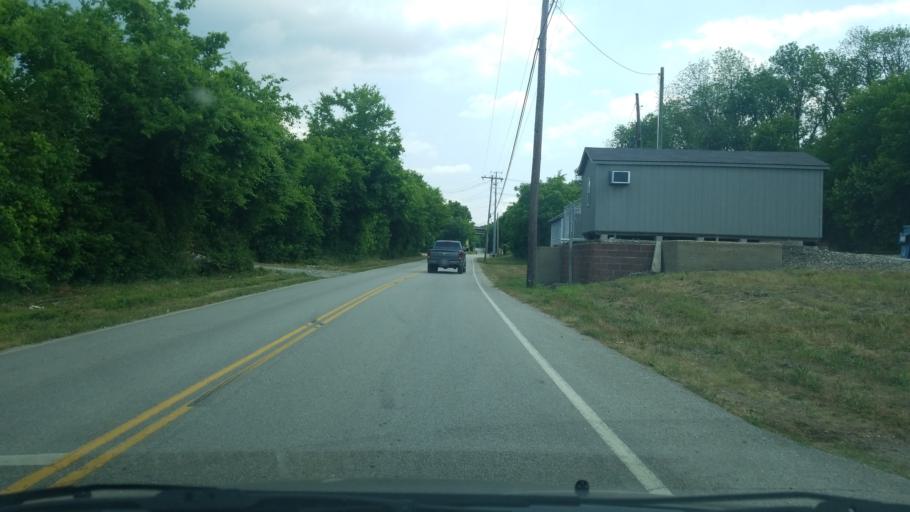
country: US
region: Tennessee
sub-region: Hamilton County
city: Soddy-Daisy
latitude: 35.2366
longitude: -85.1904
